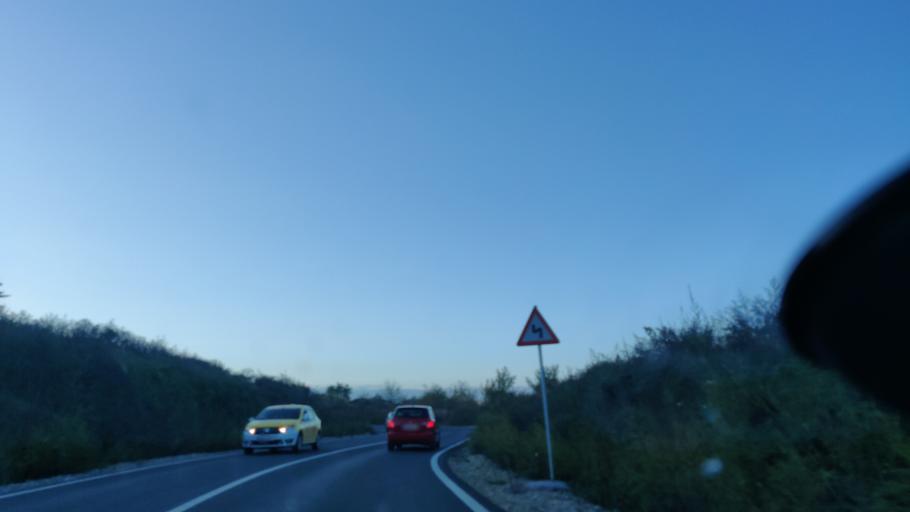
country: RO
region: Ilfov
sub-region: Comuna Chitila
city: Rudeni
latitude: 44.4701
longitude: 25.9946
